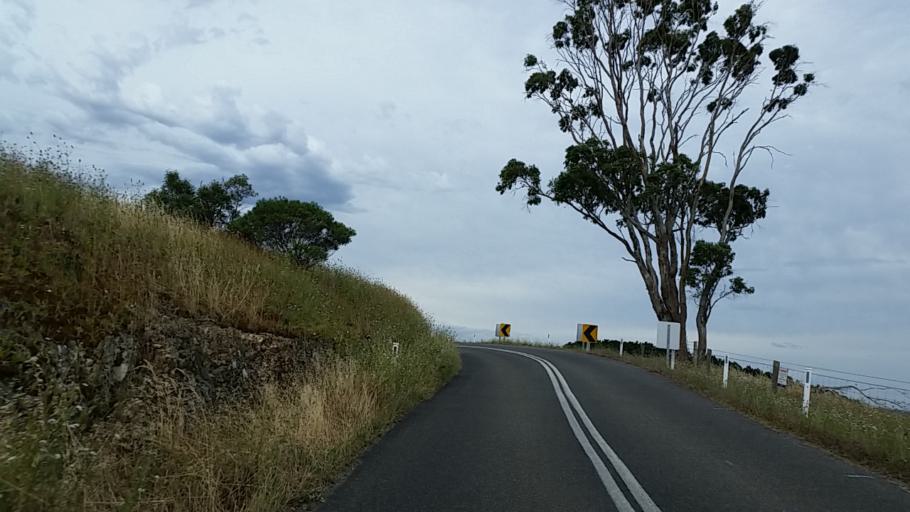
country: AU
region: South Australia
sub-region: Yankalilla
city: Normanville
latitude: -35.3981
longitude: 138.4217
